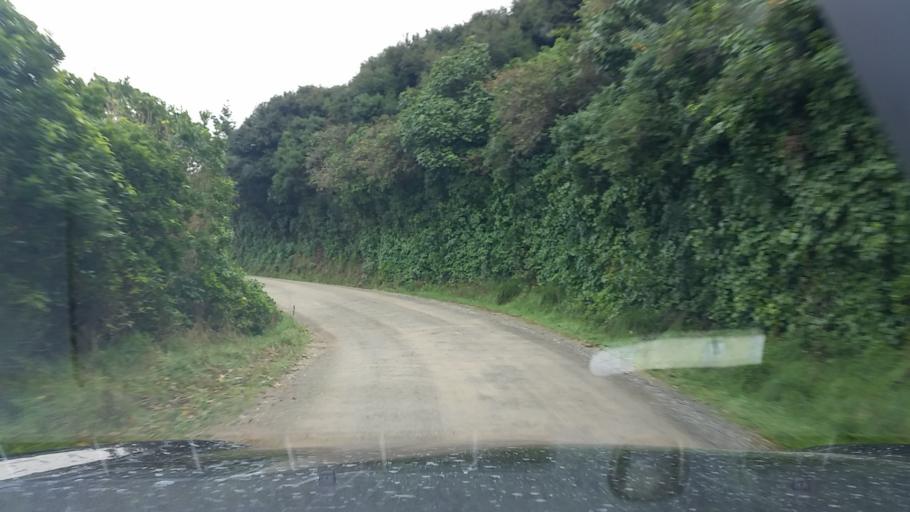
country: NZ
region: Marlborough
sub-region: Marlborough District
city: Picton
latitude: -41.1755
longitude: 174.0480
